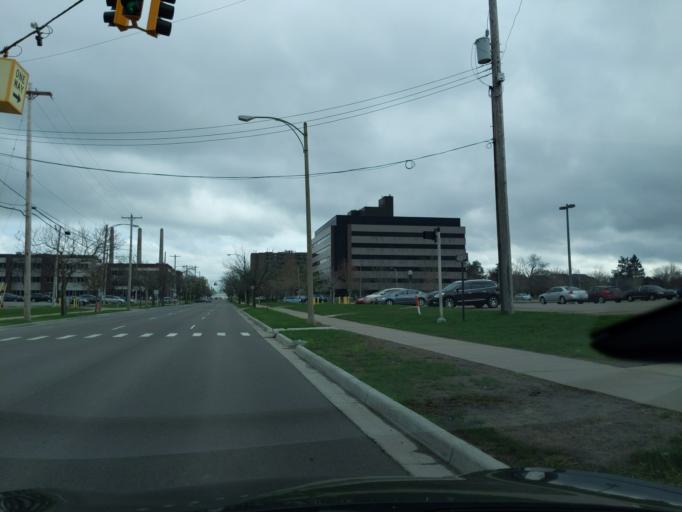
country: US
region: Michigan
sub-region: Ingham County
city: Lansing
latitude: 42.7315
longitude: -84.5601
